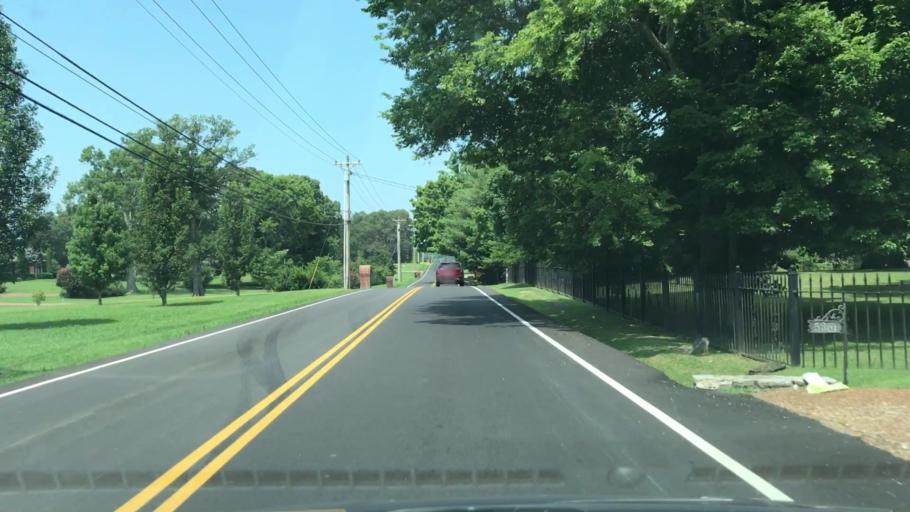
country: US
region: Tennessee
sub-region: Wilson County
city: Rural Hill
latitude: 36.1169
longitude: -86.4799
